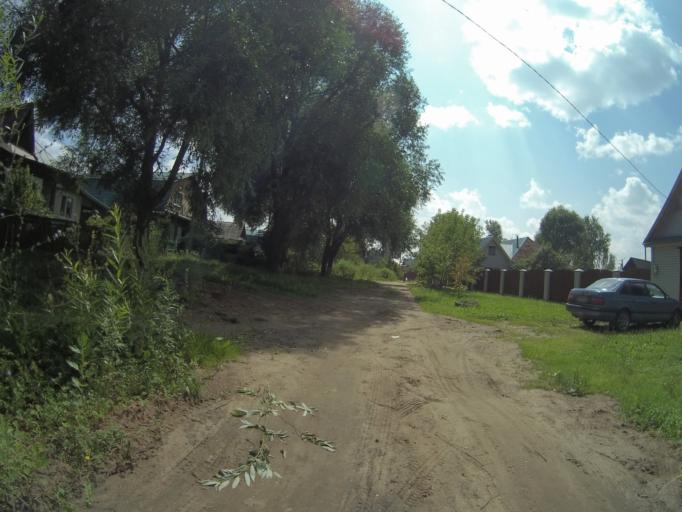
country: RU
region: Vladimir
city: Gus'-Khrustal'nyy
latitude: 55.6071
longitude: 40.6740
